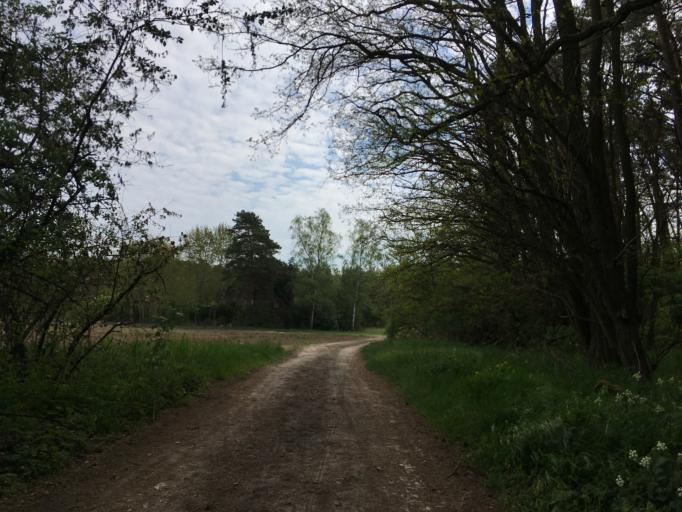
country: DE
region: Brandenburg
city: Rudnitz
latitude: 52.7110
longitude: 13.6272
